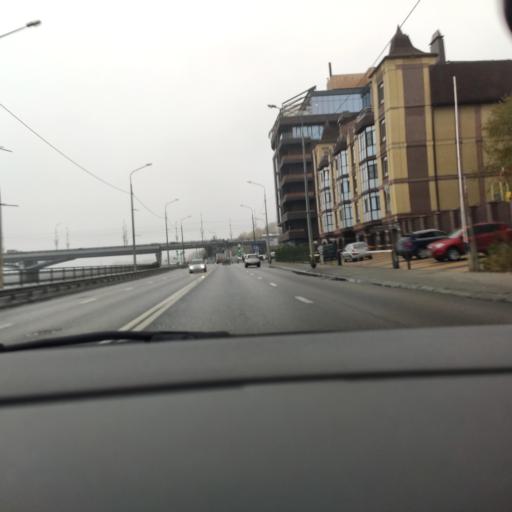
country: RU
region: Voronezj
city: Voronezh
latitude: 51.6702
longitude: 39.2230
